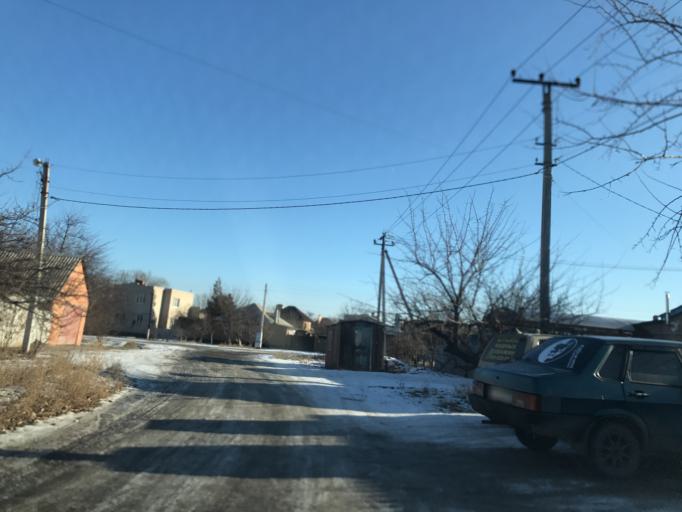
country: RU
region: Rostov
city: Kamensk-Shakhtinskiy
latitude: 48.3132
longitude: 40.2786
